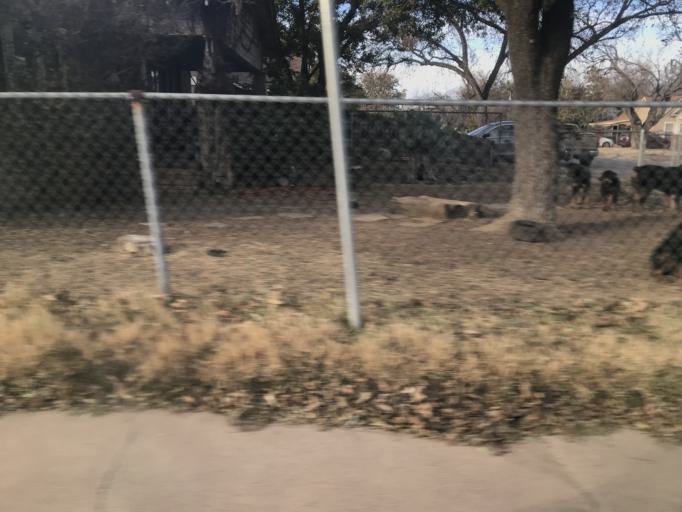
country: US
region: Texas
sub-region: Taylor County
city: Abilene
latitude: 32.4322
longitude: -99.7457
